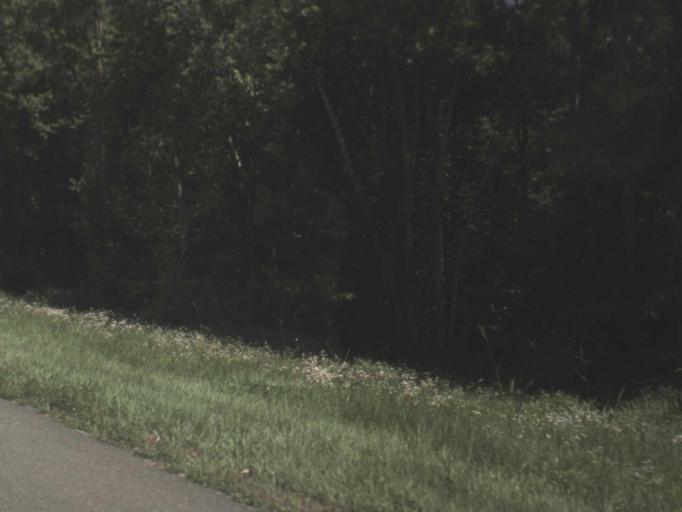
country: US
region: Florida
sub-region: Bradford County
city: Starke
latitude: 29.9201
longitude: -82.0968
